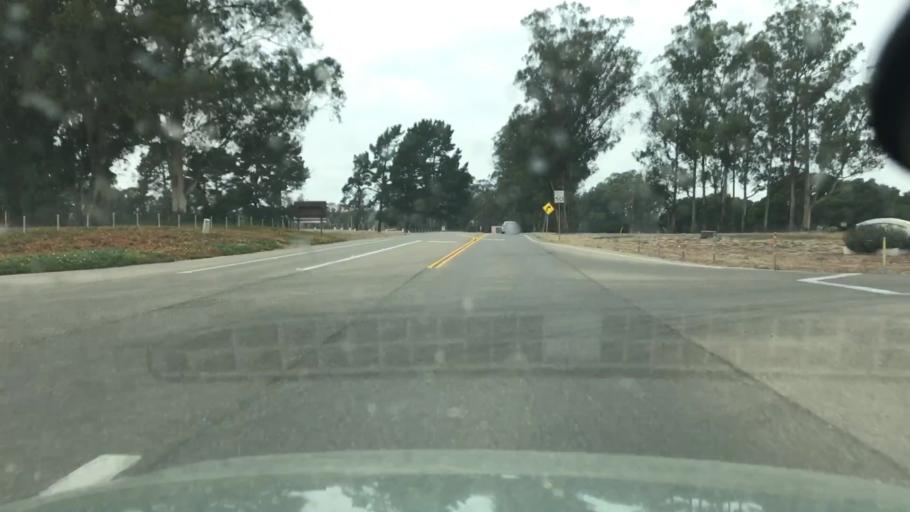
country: US
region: California
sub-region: Santa Barbara County
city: Vandenberg Village
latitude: 34.6825
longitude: -120.5008
